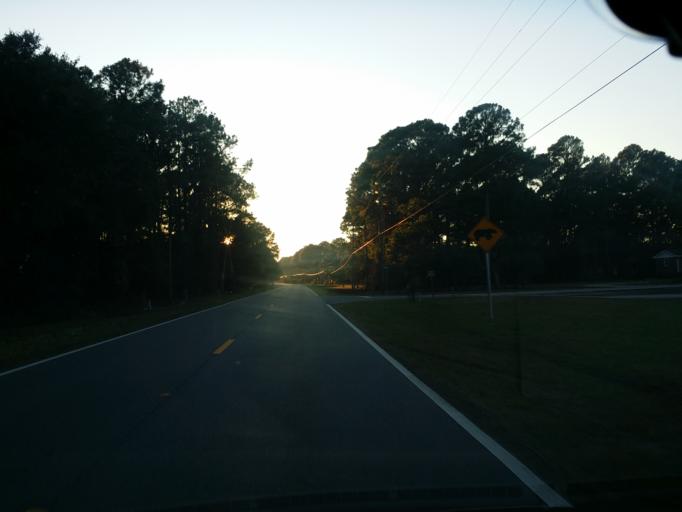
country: US
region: Florida
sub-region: Franklin County
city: Carrabelle
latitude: 29.8886
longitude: -84.5784
